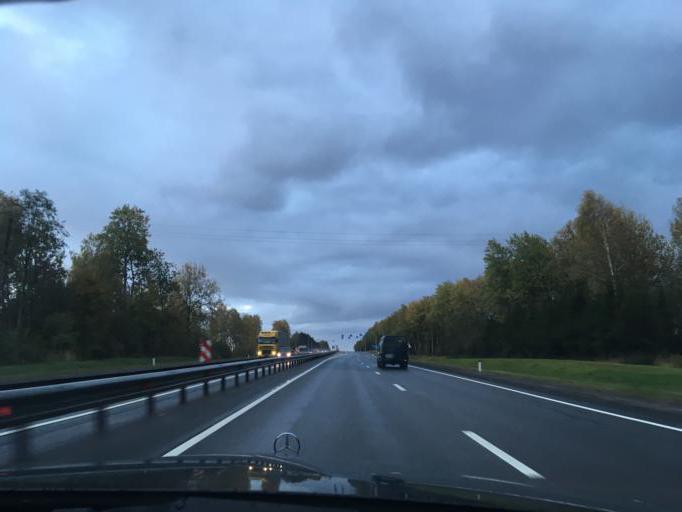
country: RU
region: Smolensk
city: Safonovo
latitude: 55.1196
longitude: 33.0669
